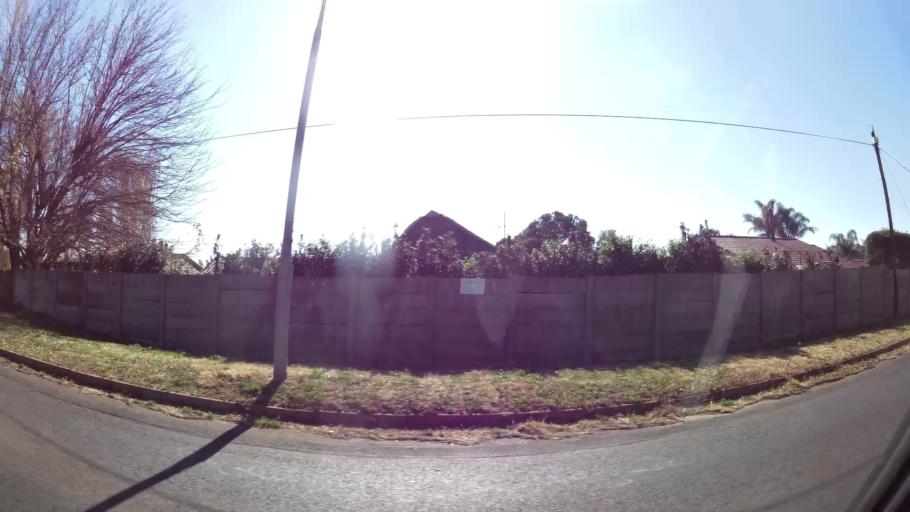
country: ZA
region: Gauteng
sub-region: City of Johannesburg Metropolitan Municipality
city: Roodepoort
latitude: -26.1231
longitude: 27.8656
